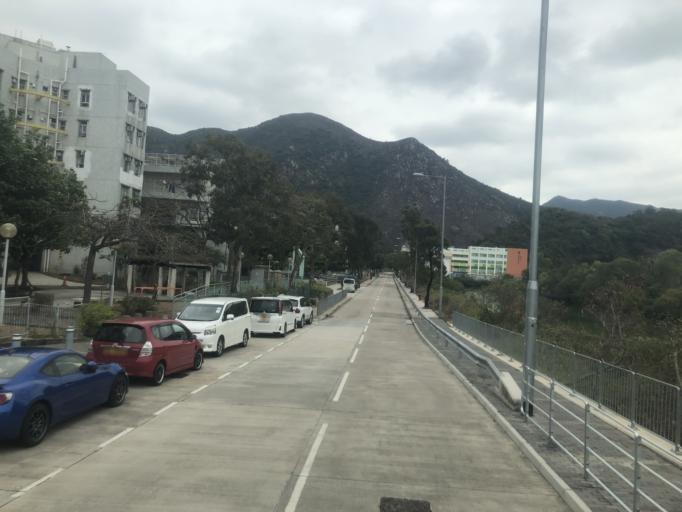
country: HK
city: Tai O
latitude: 22.2526
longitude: 113.8635
